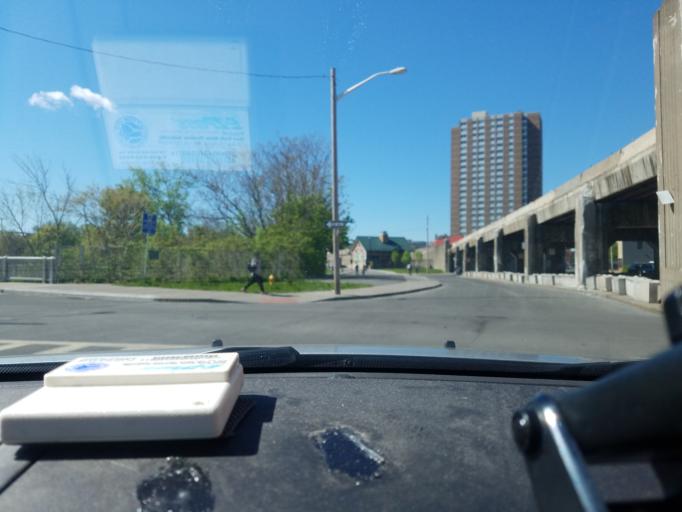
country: US
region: New York
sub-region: Onondaga County
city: Syracuse
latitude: 43.0435
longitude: -76.1536
